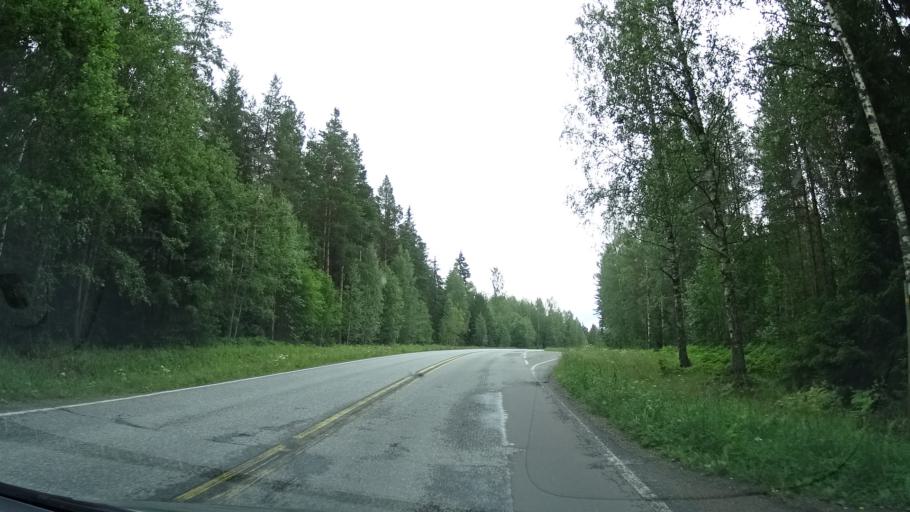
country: FI
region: Pirkanmaa
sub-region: Etelae-Pirkanmaa
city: Urjala
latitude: 61.0867
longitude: 23.5190
